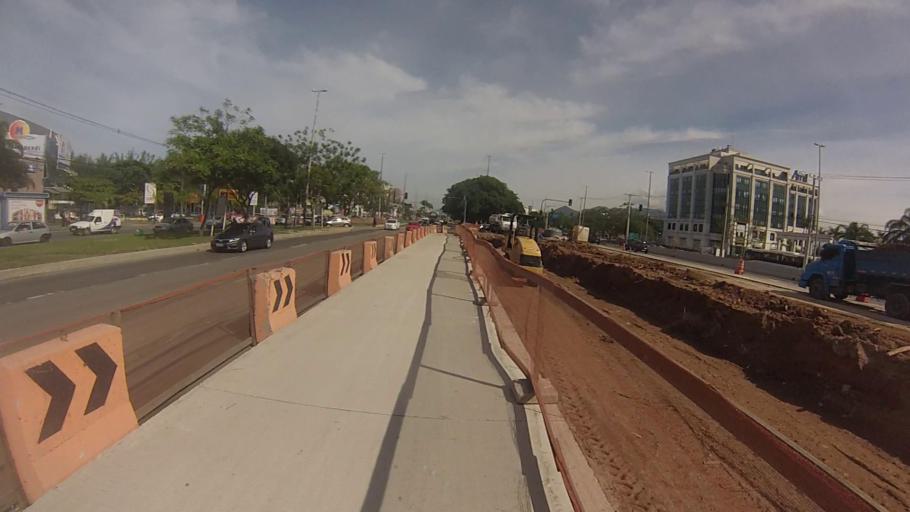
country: BR
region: Rio de Janeiro
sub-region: Rio De Janeiro
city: Rio de Janeiro
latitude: -23.0000
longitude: -43.3529
